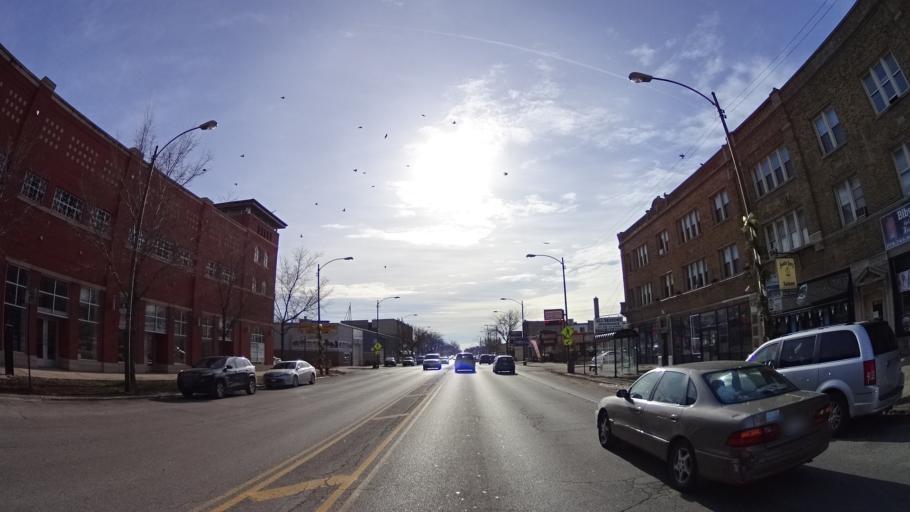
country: US
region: Illinois
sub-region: Cook County
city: Lincolnwood
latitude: 41.9965
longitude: -87.6899
